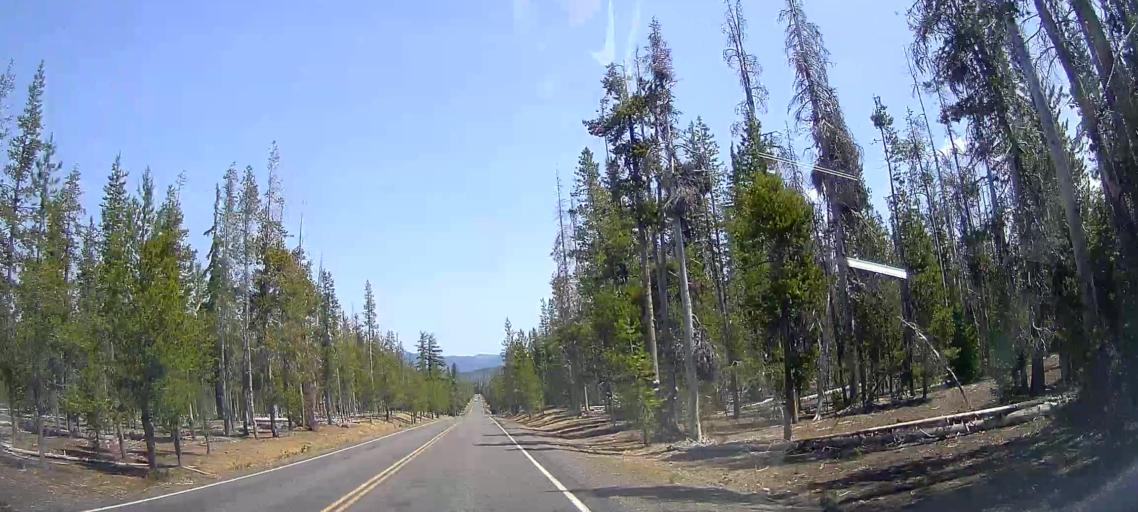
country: US
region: Oregon
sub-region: Jackson County
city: Shady Cove
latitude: 43.0153
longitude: -122.1271
